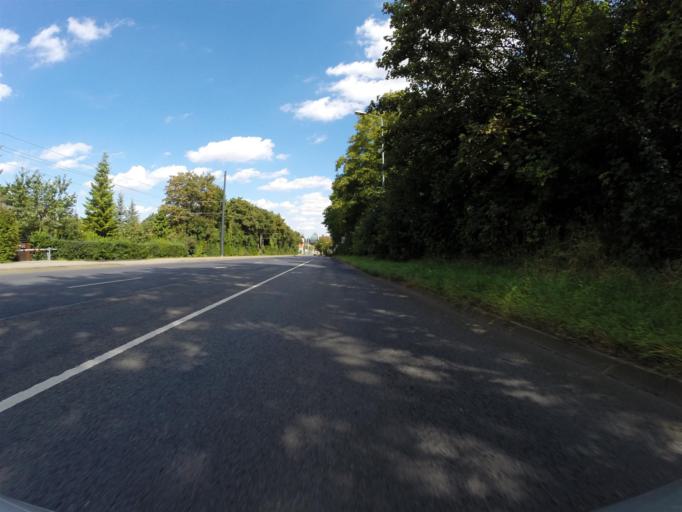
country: DE
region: Thuringia
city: Erfurt
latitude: 50.9696
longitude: 11.0066
